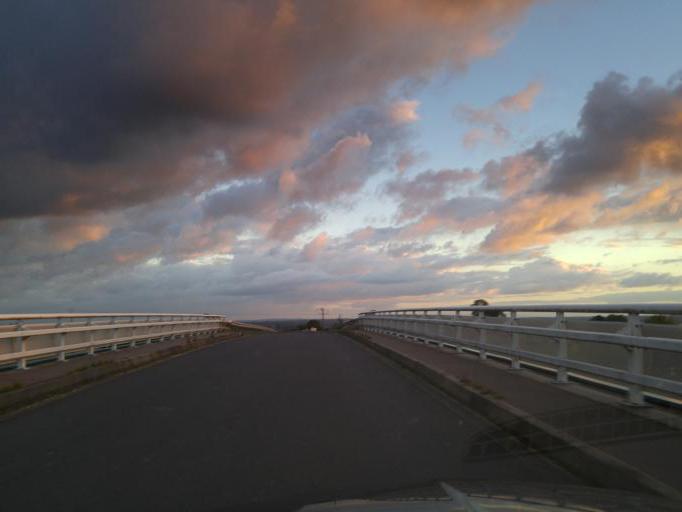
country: FR
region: Lower Normandy
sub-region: Departement du Calvados
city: Grandcamp-Maisy
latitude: 49.3417
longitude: -0.9802
